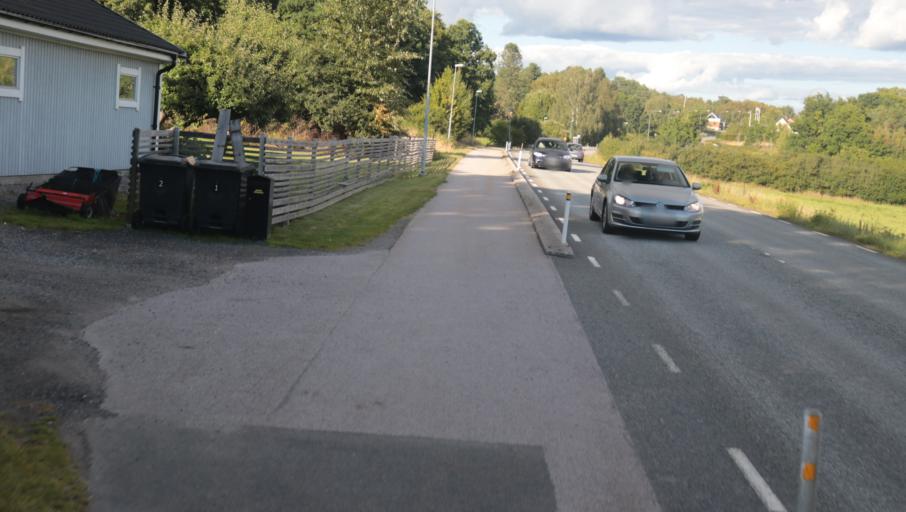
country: SE
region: Blekinge
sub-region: Karlshamns Kommun
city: Karlshamn
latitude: 56.1776
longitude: 14.9053
